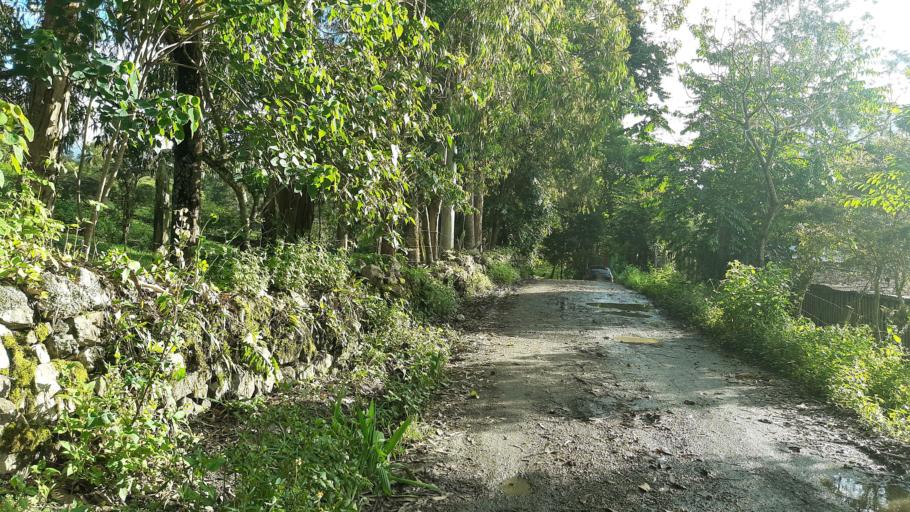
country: CO
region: Boyaca
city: Garagoa
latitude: 5.0937
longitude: -73.3592
